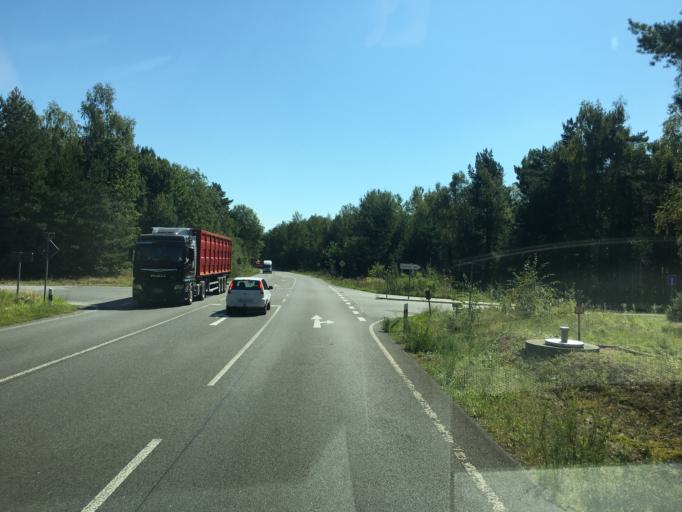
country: DE
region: Brandenburg
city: Welzow
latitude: 51.5650
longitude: 14.1102
